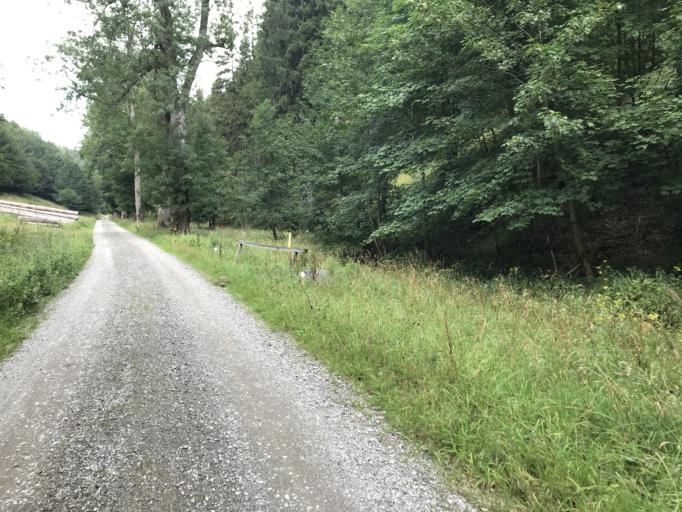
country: DE
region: Lower Saxony
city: Sankt Andreasberg
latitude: 51.6896
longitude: 10.5319
